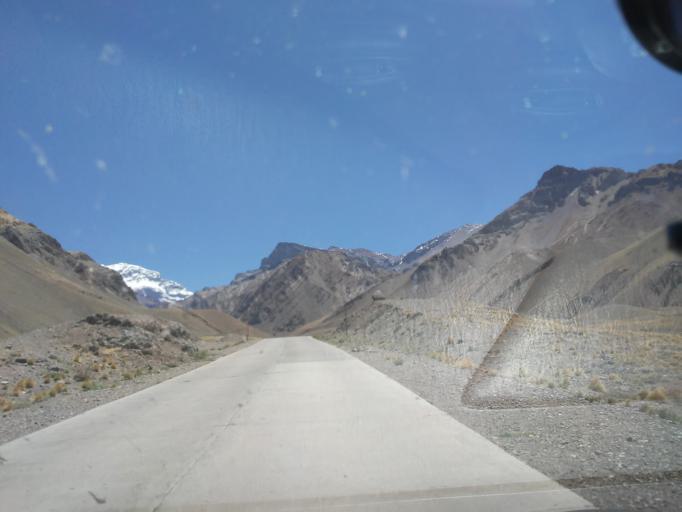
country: CL
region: Valparaiso
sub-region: Provincia de Los Andes
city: Los Andes
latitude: -32.8195
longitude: -69.9422
